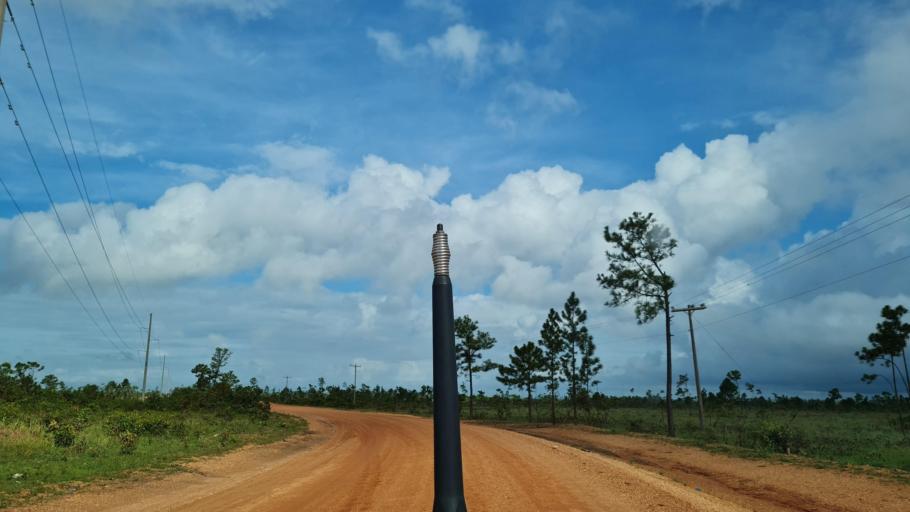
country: NI
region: Atlantico Norte (RAAN)
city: Puerto Cabezas
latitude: 14.1680
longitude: -83.4728
